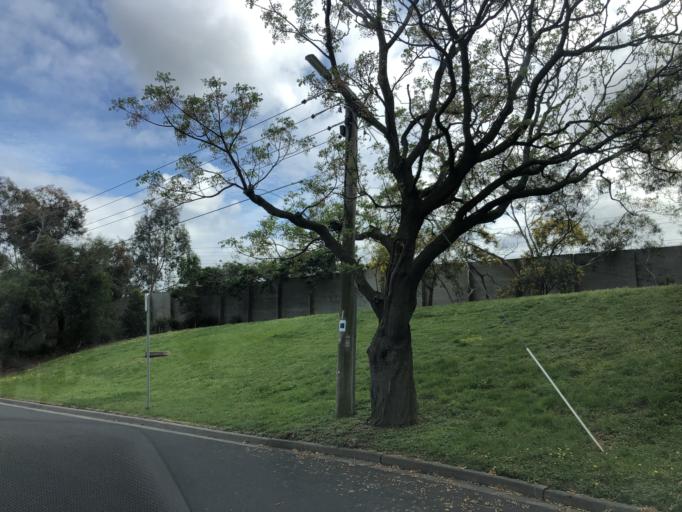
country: AU
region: Victoria
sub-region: Monash
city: Chadstone
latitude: -37.8860
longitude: 145.0988
